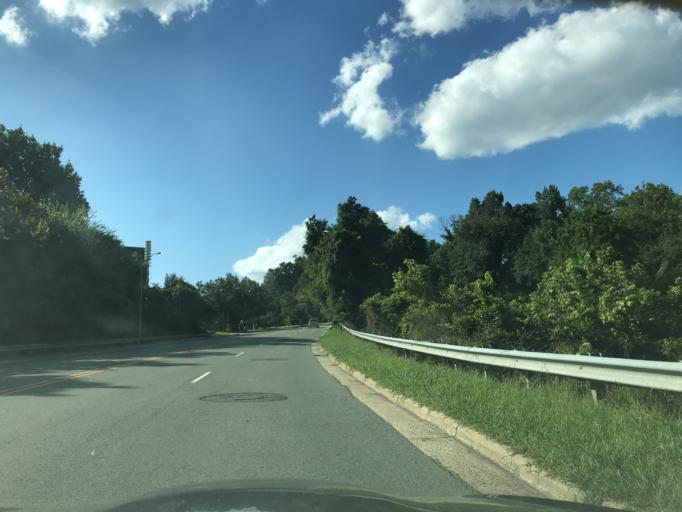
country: US
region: North Carolina
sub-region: Orange County
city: Chapel Hill
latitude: 35.9016
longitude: -79.0410
